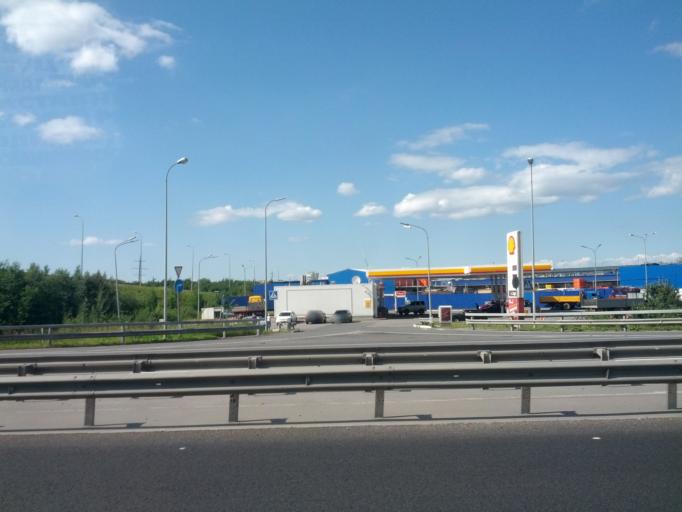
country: RU
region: Leningrad
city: Rybatskoye
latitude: 59.8875
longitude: 30.5065
